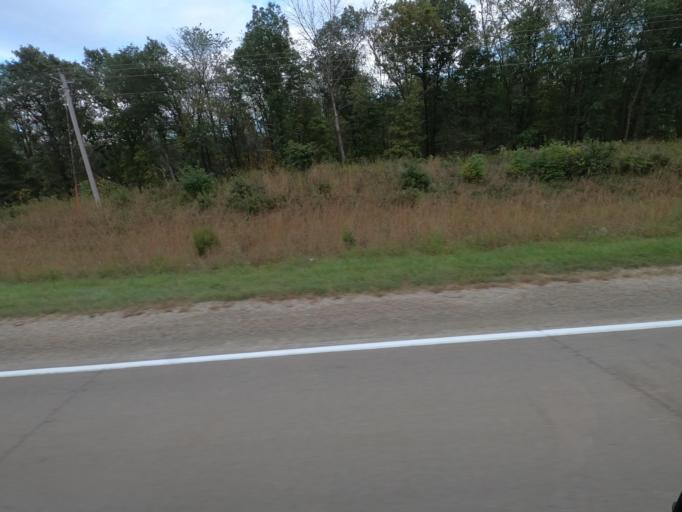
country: US
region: Iowa
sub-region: Henry County
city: Mount Pleasant
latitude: 40.7935
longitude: -91.7050
